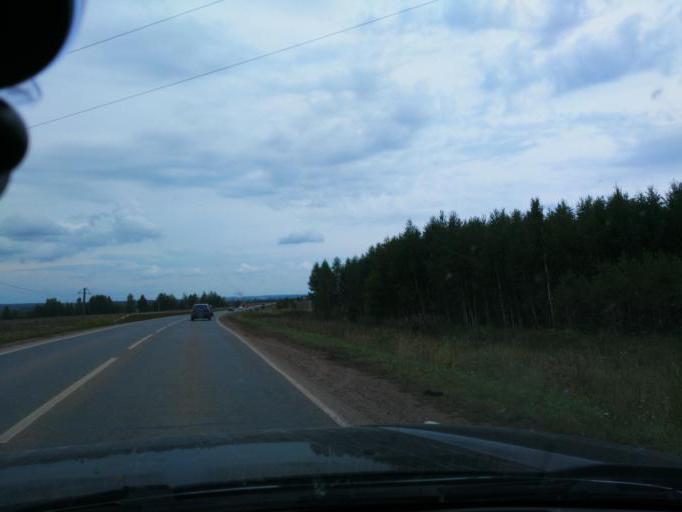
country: RU
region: Perm
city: Chernushka
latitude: 56.5102
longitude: 55.9612
